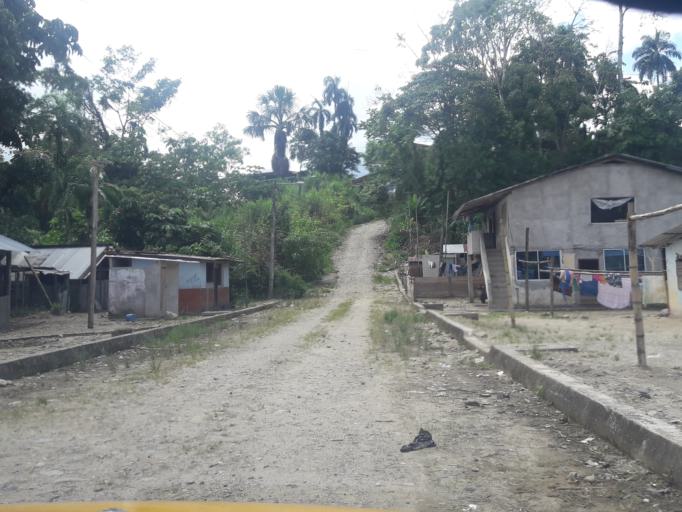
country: EC
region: Napo
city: Tena
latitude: -1.0049
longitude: -77.8222
